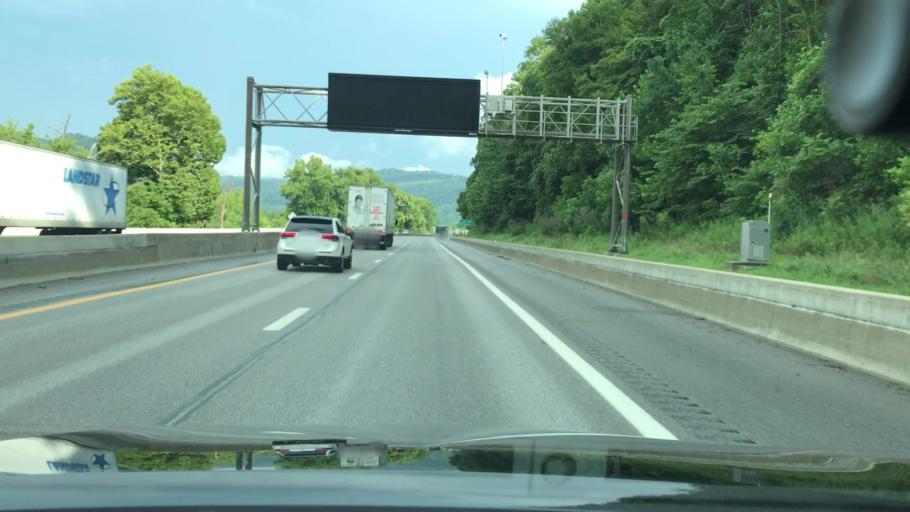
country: US
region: West Virginia
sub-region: Kanawha County
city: Chesapeake
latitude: 38.2113
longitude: -81.5256
